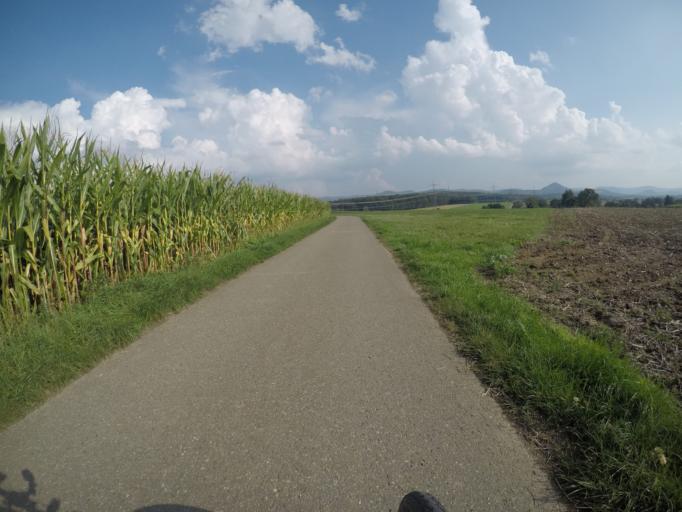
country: DE
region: Baden-Wuerttemberg
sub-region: Tuebingen Region
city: Pliezhausen
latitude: 48.5550
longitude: 9.2370
